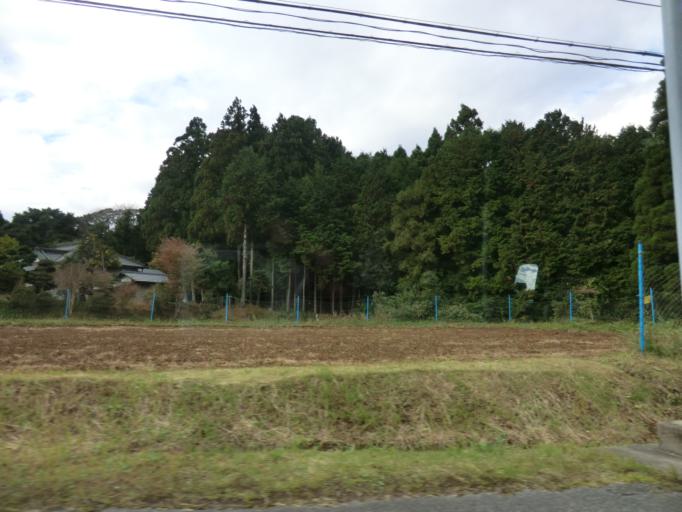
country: JP
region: Chiba
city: Kawaguchi
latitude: 35.1834
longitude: 140.0613
